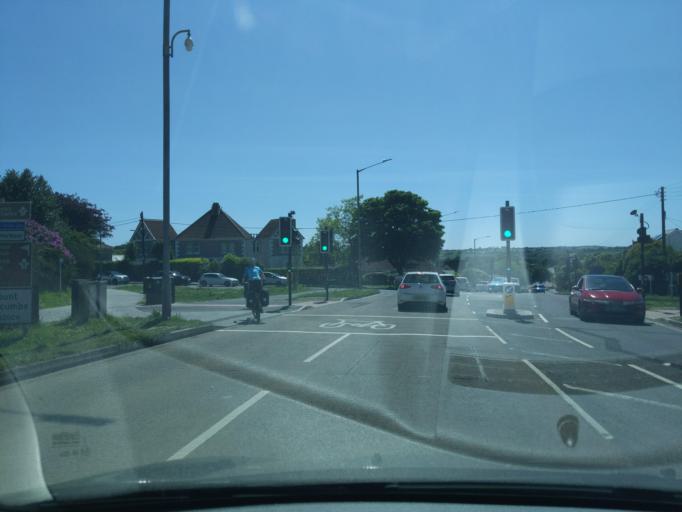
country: GB
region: England
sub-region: Cornwall
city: St Austell
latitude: 50.3368
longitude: -4.7716
